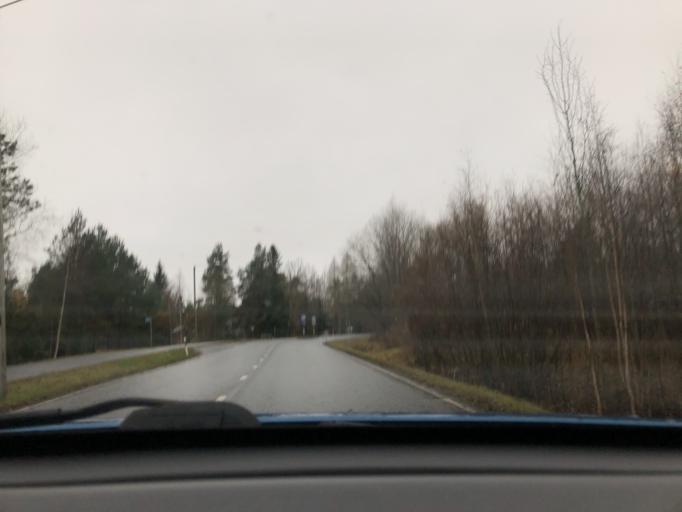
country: FI
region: Pirkanmaa
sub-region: Tampere
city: Kangasala
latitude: 61.4531
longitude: 24.0339
